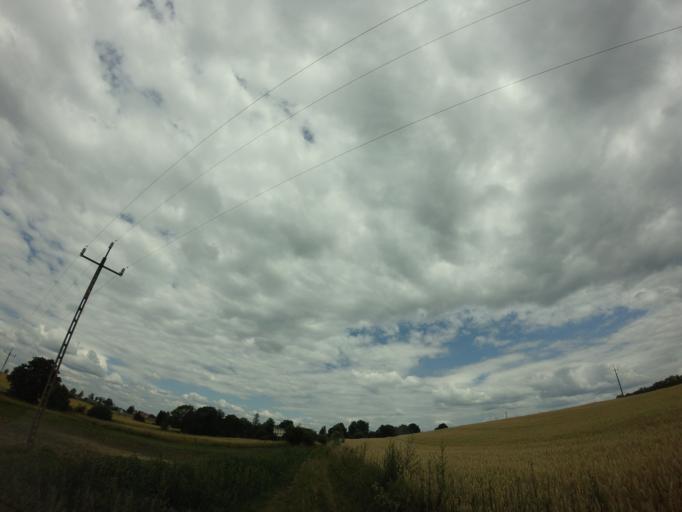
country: PL
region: West Pomeranian Voivodeship
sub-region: Powiat choszczenski
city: Recz
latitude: 53.1834
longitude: 15.5789
